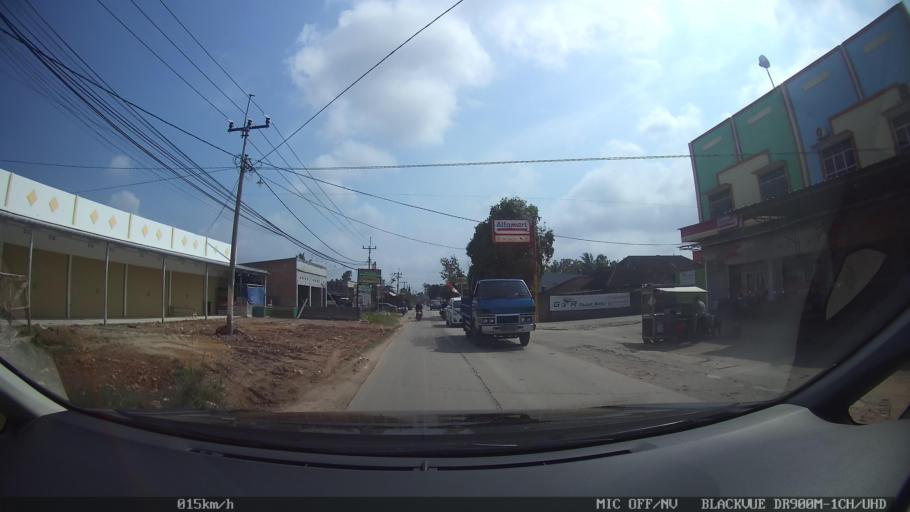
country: ID
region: Lampung
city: Kedaton
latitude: -5.3480
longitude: 105.2663
